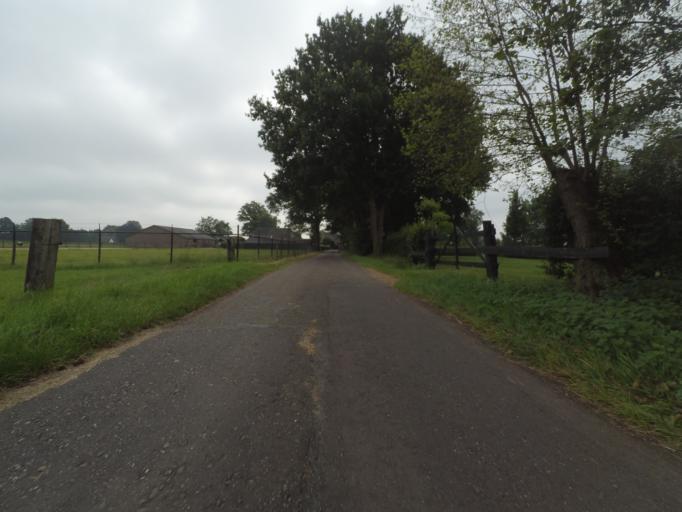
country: NL
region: Gelderland
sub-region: Gemeente Barneveld
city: Kootwijkerbroek
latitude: 52.1224
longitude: 5.6798
